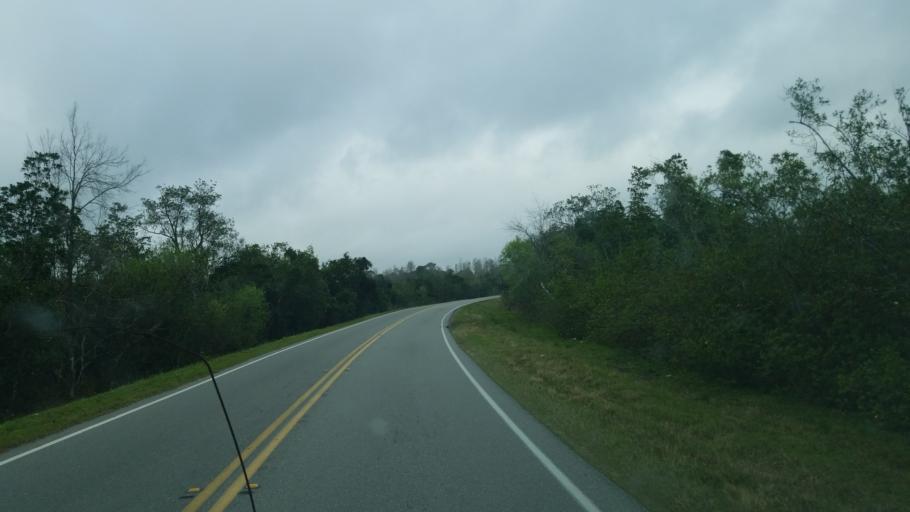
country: US
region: Florida
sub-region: Polk County
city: Polk City
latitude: 28.2581
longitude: -81.8041
